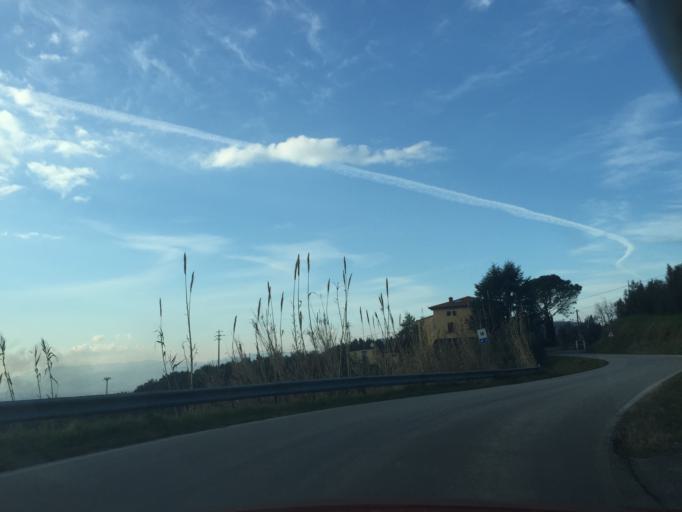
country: IT
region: Tuscany
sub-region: Province of Florence
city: Vinci
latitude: 43.8181
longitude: 10.9257
